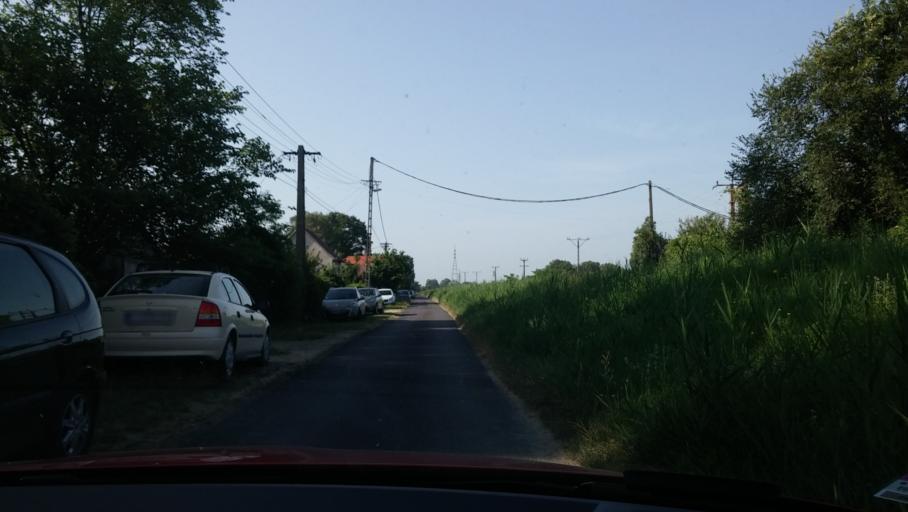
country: HU
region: Pest
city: Rackeve
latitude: 47.1874
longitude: 18.9485
